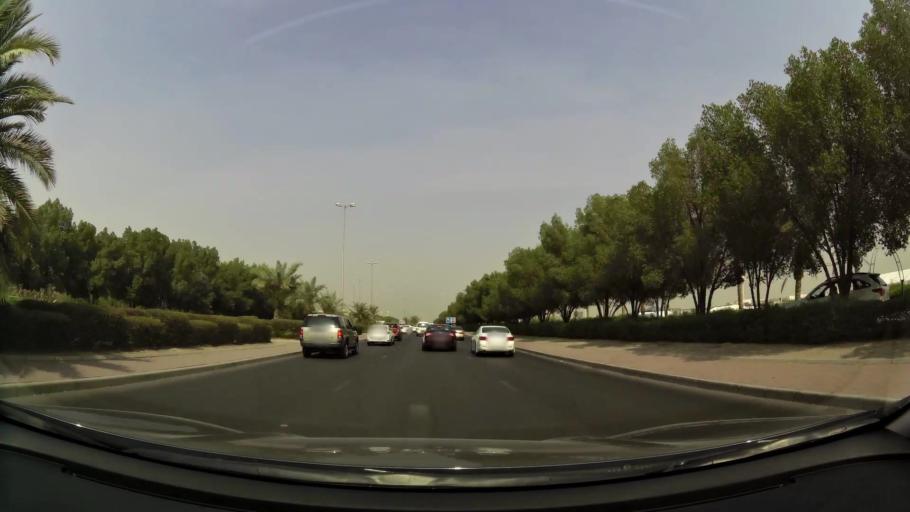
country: KW
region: Al Asimah
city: Ar Rabiyah
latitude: 29.2830
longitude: 47.9067
